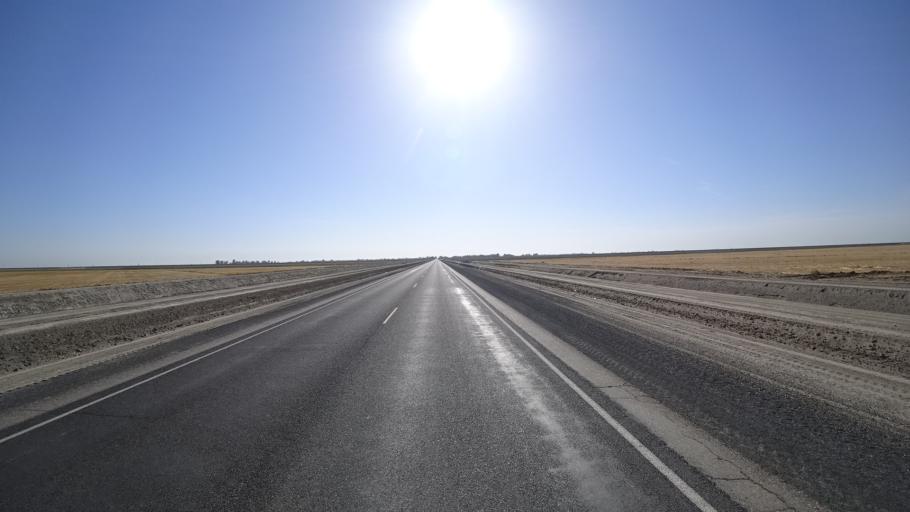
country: US
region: California
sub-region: Kings County
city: Corcoran
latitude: 36.0980
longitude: -119.6201
